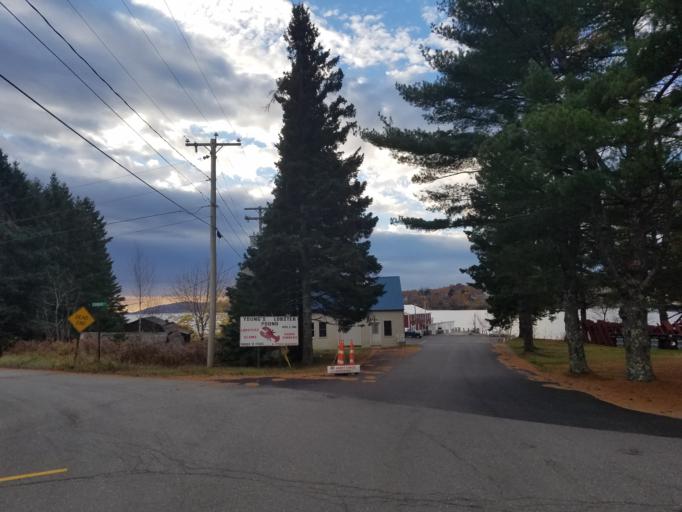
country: US
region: Maine
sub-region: Waldo County
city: Belfast
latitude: 44.4314
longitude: -68.9965
